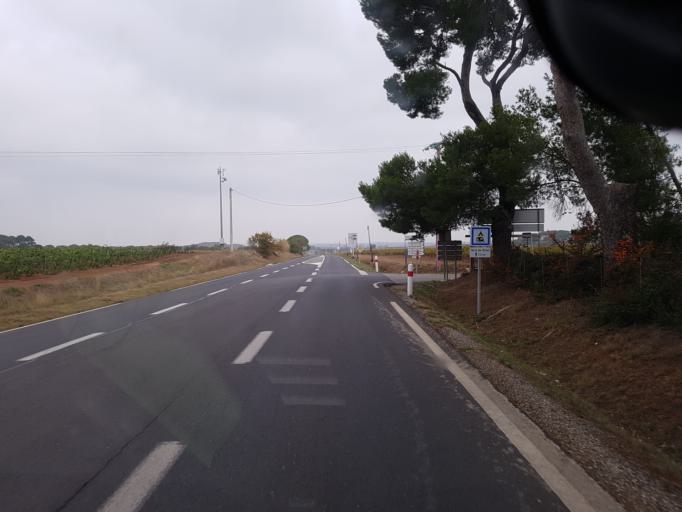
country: FR
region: Languedoc-Roussillon
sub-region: Departement de l'Herault
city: Pinet
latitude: 43.3900
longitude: 3.5377
